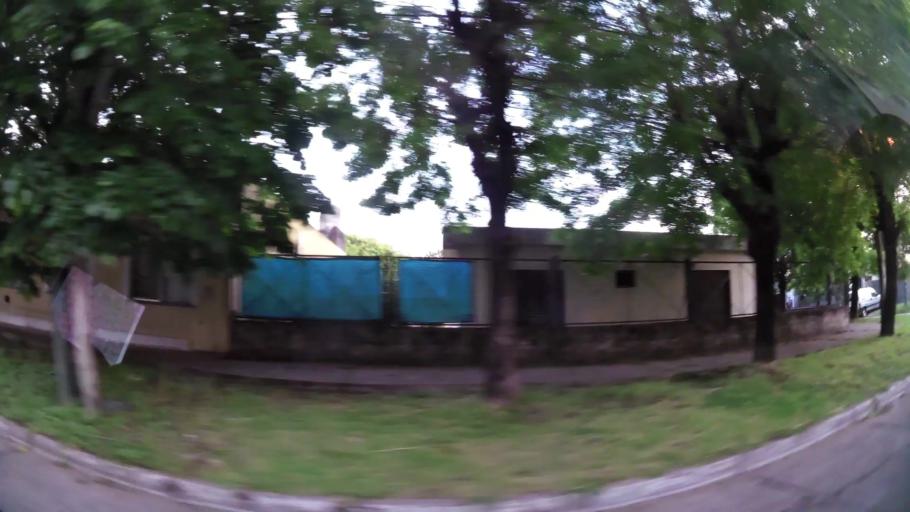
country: AR
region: Buenos Aires
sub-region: Partido de Lomas de Zamora
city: Lomas de Zamora
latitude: -34.7641
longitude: -58.3709
